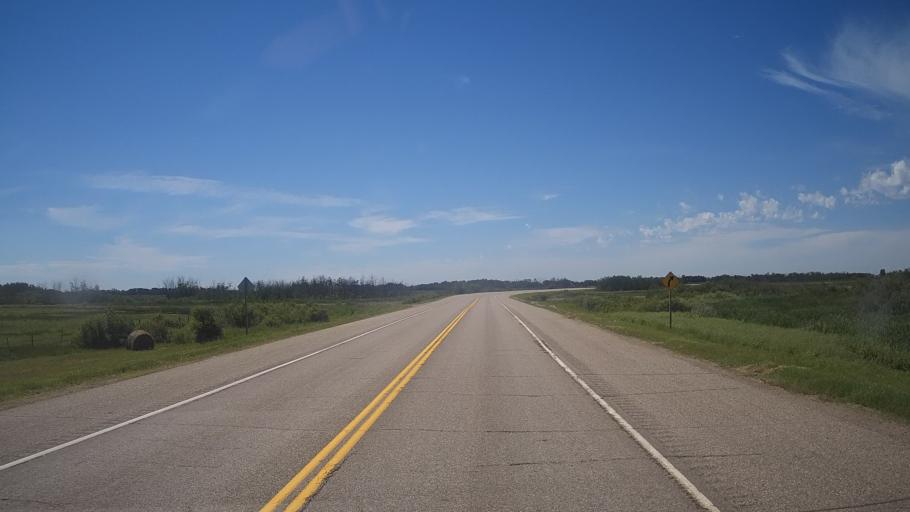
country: CA
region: Saskatchewan
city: Langenburg
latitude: 50.7715
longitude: -101.4916
